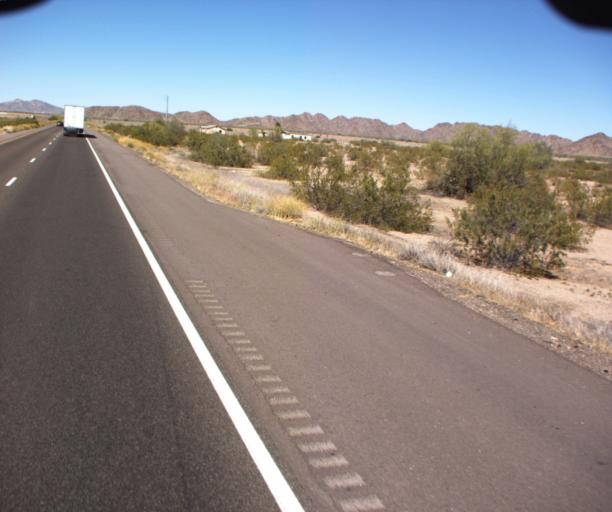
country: US
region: Arizona
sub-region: Maricopa County
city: Gila Bend
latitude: 33.1434
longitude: -112.6500
